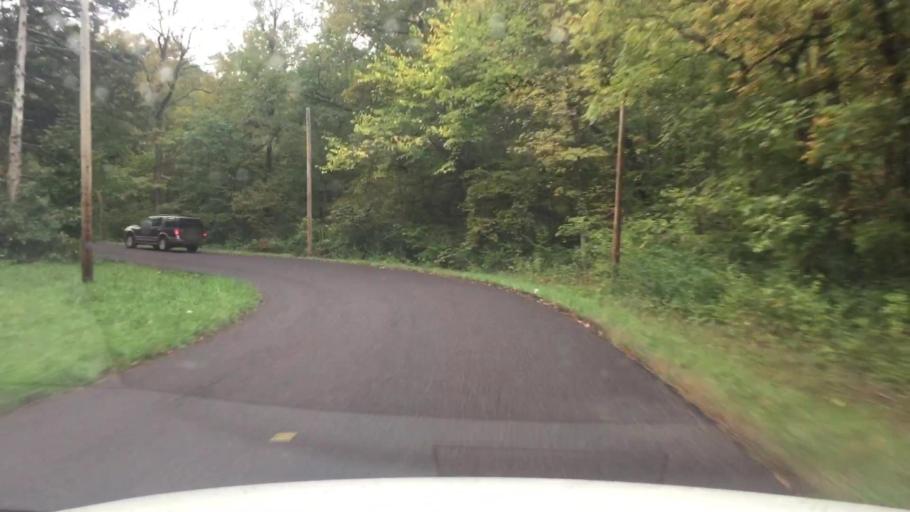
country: US
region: Missouri
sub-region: Boone County
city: Ashland
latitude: 38.8116
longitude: -92.2779
